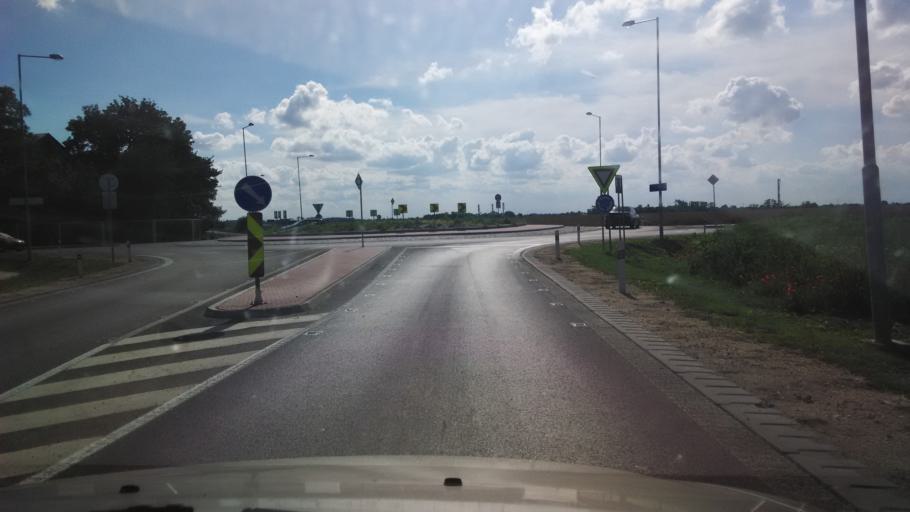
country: SK
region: Nitriansky
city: Surany
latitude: 48.0856
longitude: 18.1529
